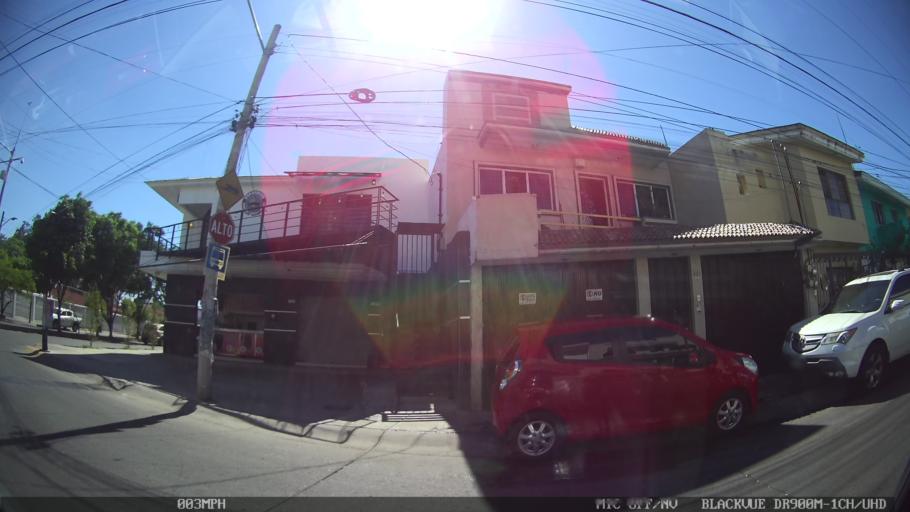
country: MX
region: Jalisco
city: Tlaquepaque
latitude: 20.6476
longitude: -103.2900
